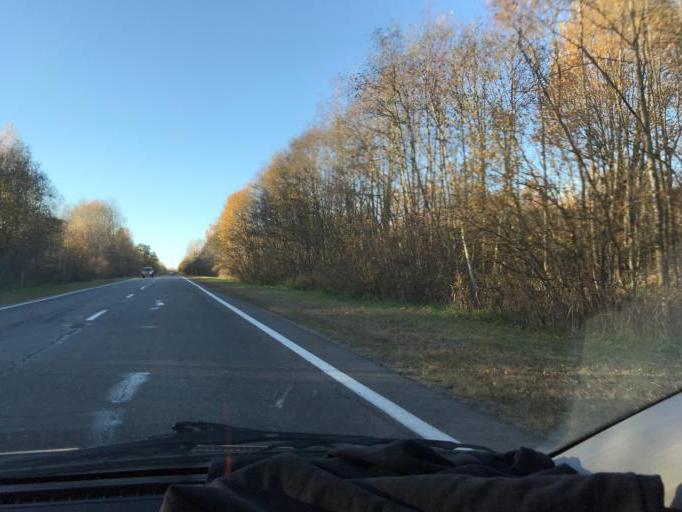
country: BY
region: Vitebsk
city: Vitebsk
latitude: 55.3538
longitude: 30.1919
